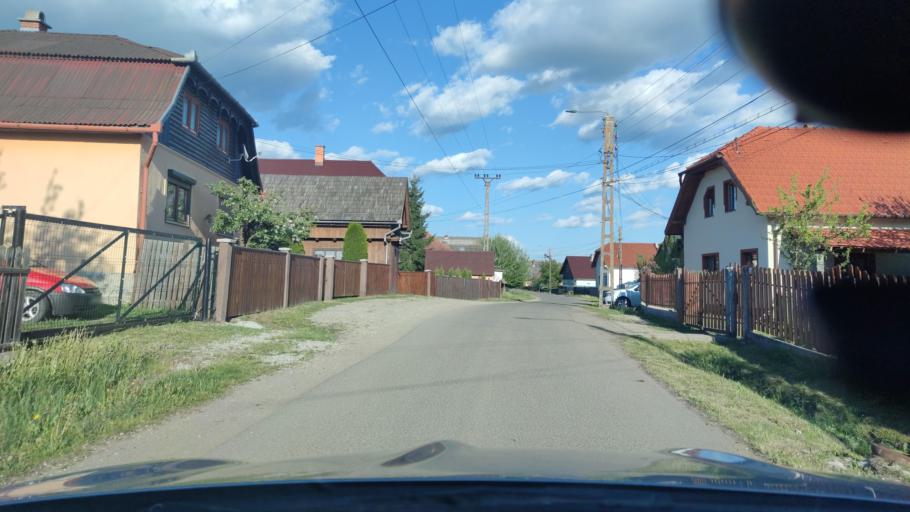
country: RO
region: Harghita
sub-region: Comuna Remetea
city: Remetea
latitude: 46.7974
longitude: 25.4370
